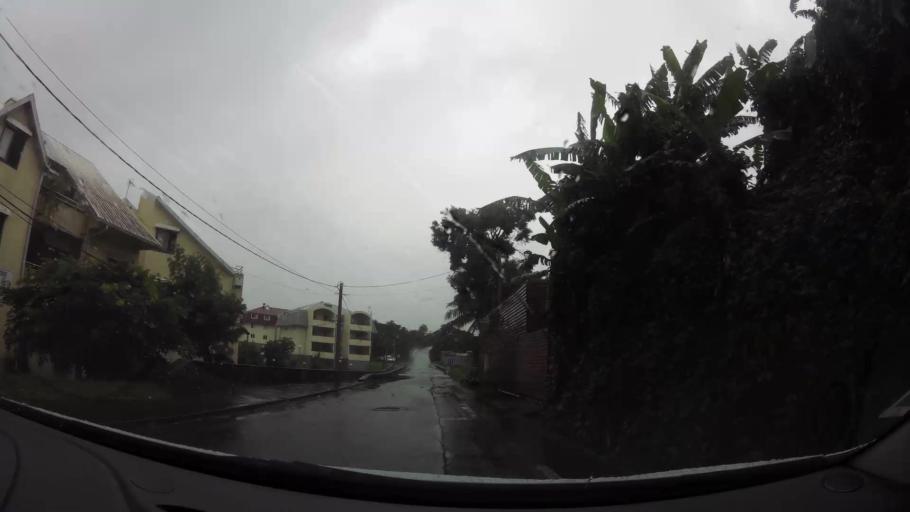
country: RE
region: Reunion
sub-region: Reunion
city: Saint-Andre
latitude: -20.9627
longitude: 55.6462
